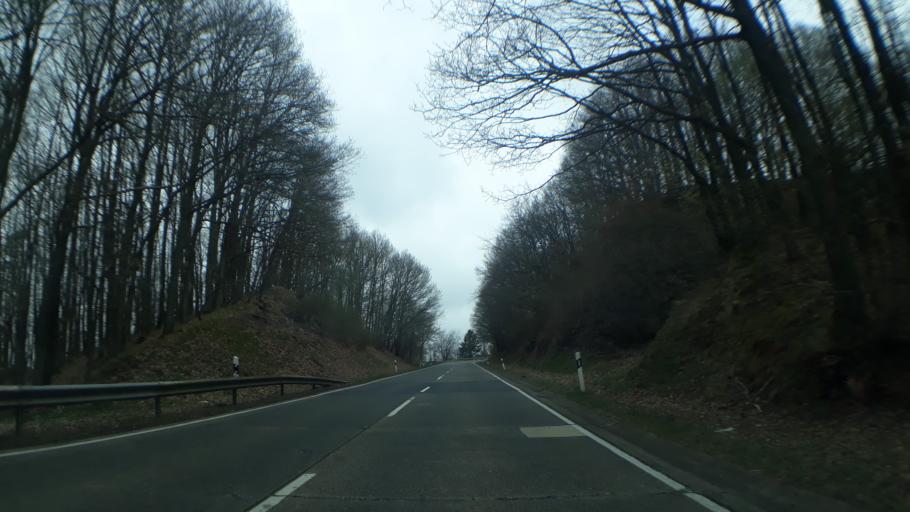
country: DE
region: North Rhine-Westphalia
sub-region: Regierungsbezirk Koln
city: Schleiden
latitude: 50.5452
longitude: 6.4725
